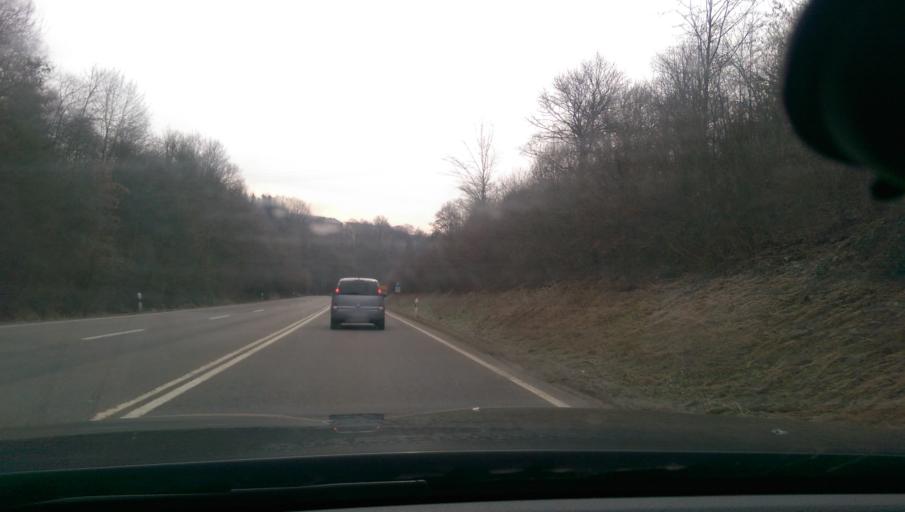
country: DE
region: Bavaria
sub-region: Lower Bavaria
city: Passau
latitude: 48.5804
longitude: 13.4227
